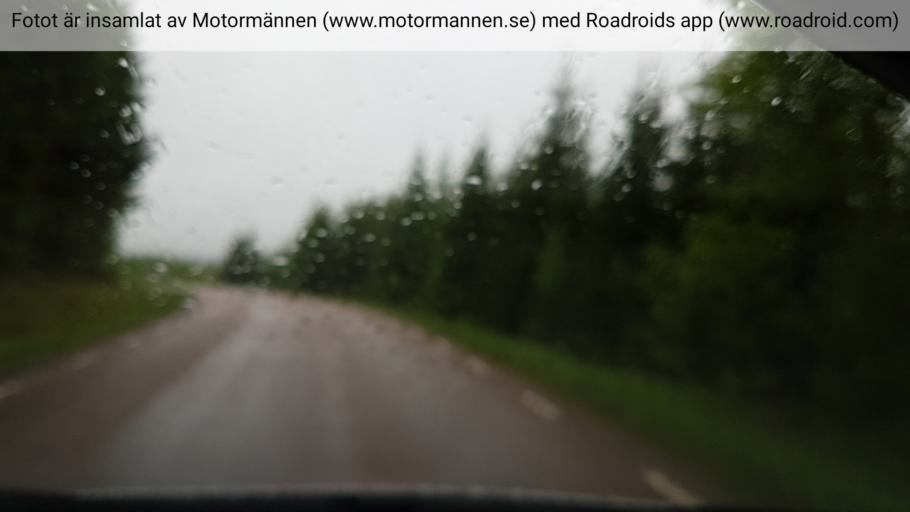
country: SE
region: Vaestra Goetaland
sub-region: Ulricehamns Kommun
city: Ulricehamn
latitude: 57.8313
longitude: 13.4981
